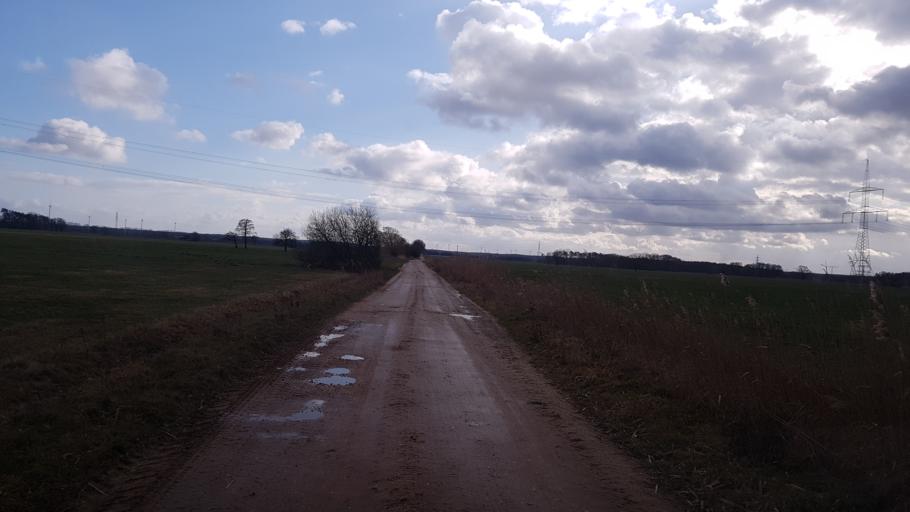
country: DE
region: Brandenburg
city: Sallgast
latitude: 51.6311
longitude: 13.8566
